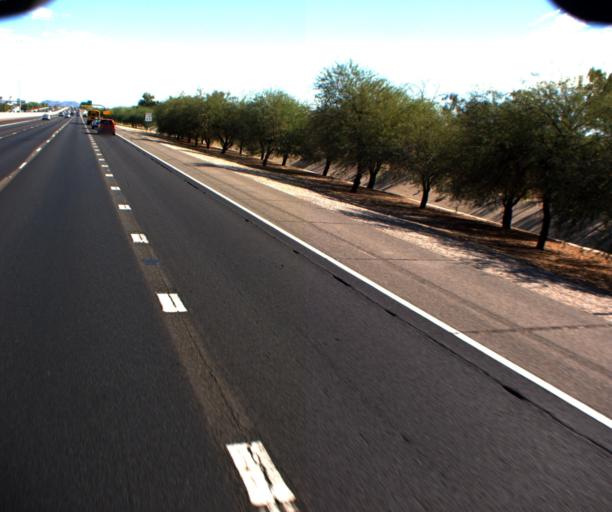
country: US
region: Arizona
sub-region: Maricopa County
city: Sun City
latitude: 33.6035
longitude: -112.2518
